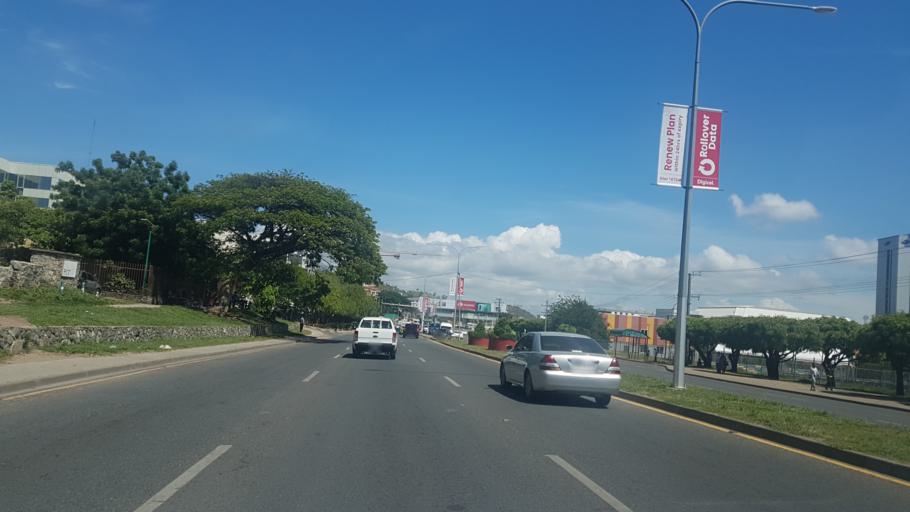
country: PG
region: National Capital
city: Port Moresby
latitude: -9.4421
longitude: 147.1815
